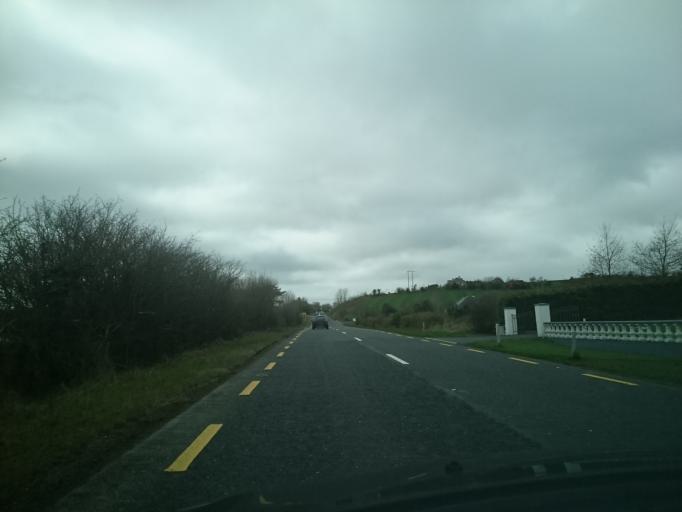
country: IE
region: Connaught
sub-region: Maigh Eo
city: Westport
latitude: 53.8062
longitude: -9.4503
